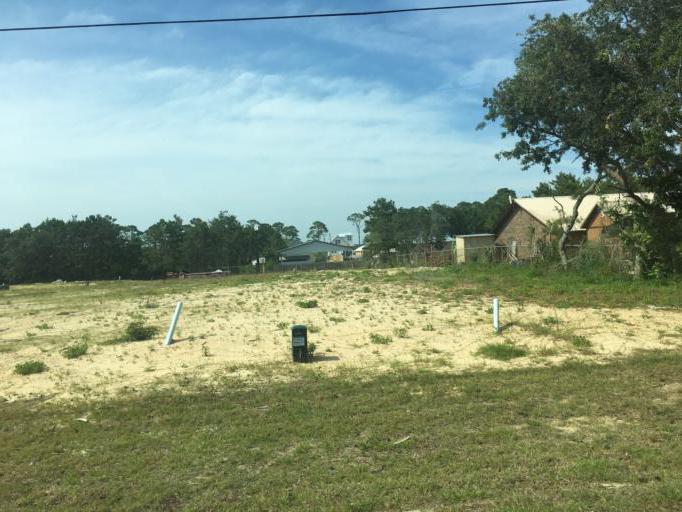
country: US
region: Florida
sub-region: Bay County
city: Laguna Beach
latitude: 30.2673
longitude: -85.9687
